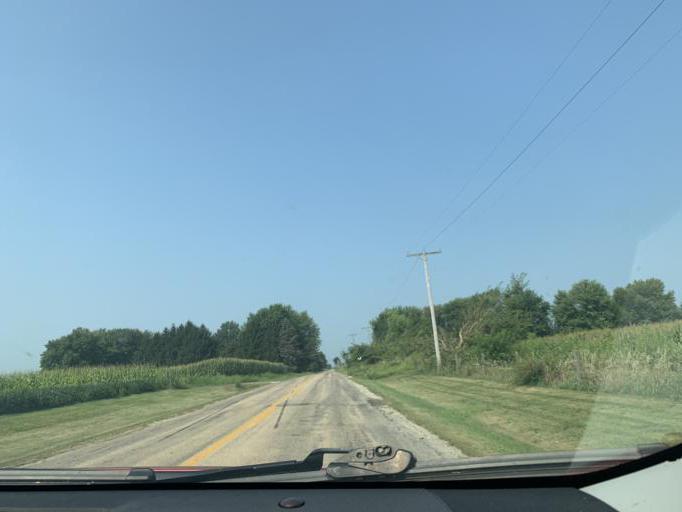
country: US
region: Illinois
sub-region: Carroll County
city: Milledgeville
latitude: 41.8480
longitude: -89.8363
